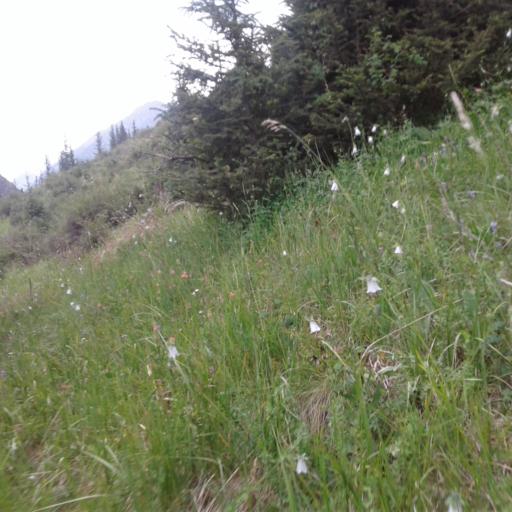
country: KG
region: Naryn
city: Naryn
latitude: 41.4543
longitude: 76.4528
